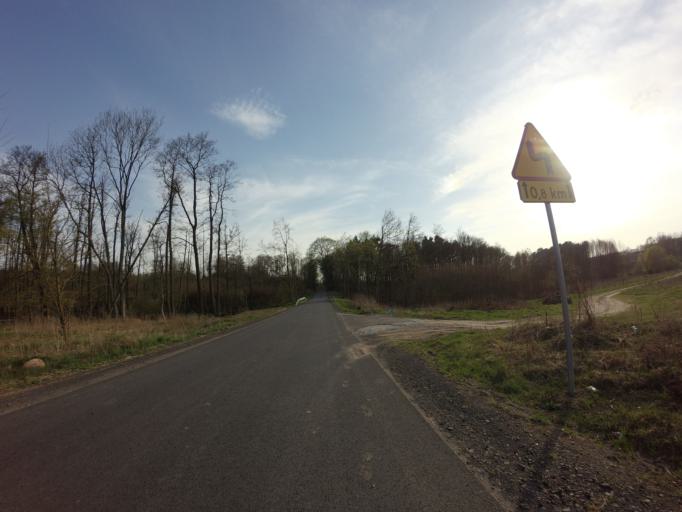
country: PL
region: West Pomeranian Voivodeship
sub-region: Powiat choszczenski
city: Recz
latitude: 53.1871
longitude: 15.5036
